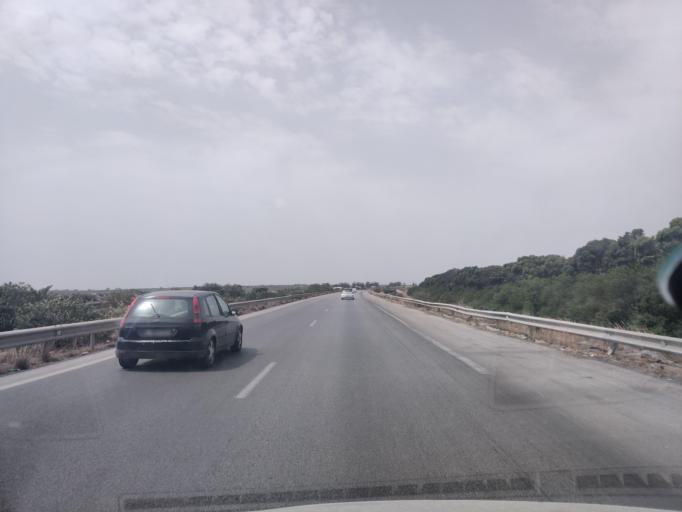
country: TN
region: Susah
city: Sidi Bou Ali
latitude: 35.9707
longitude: 10.4648
